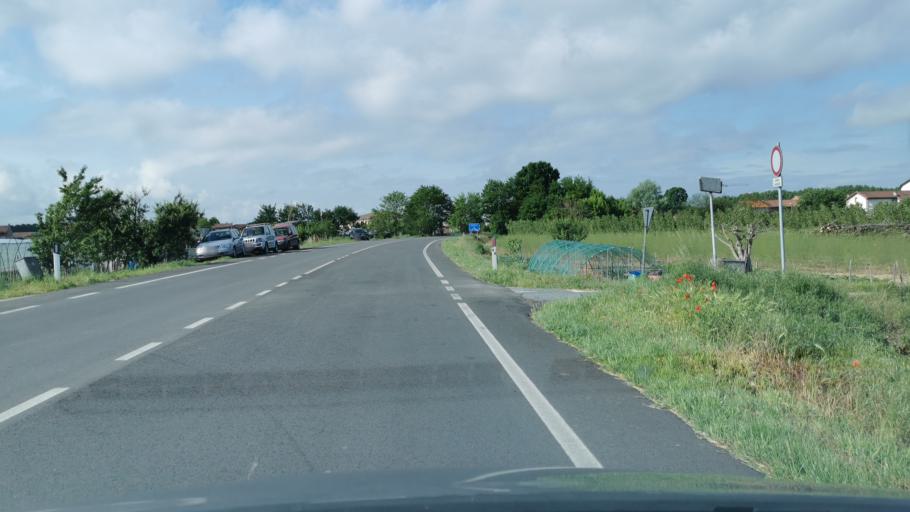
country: IT
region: Piedmont
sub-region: Provincia di Torino
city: Santena
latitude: 44.9428
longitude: 7.7813
